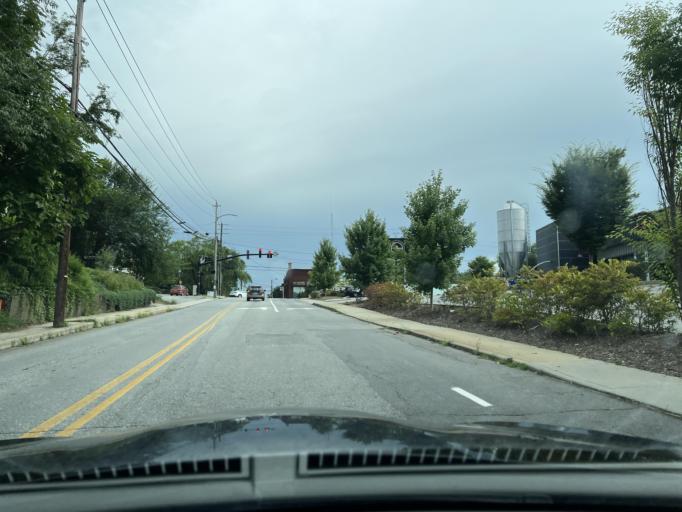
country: US
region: North Carolina
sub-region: Buncombe County
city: Asheville
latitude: 35.5784
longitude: -82.5747
